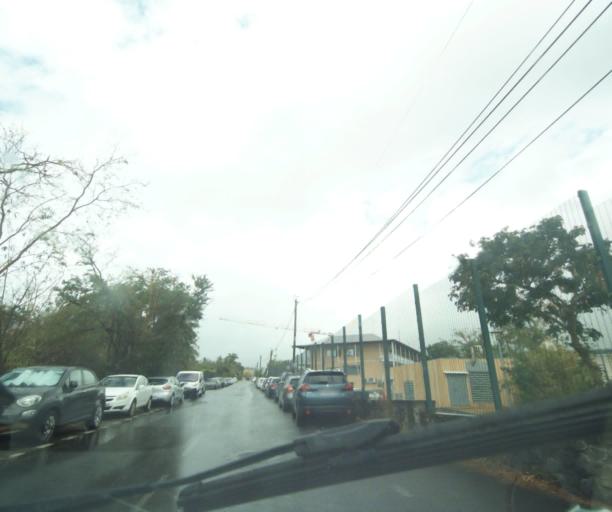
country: RE
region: Reunion
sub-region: Reunion
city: Le Port
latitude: -20.9750
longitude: 55.3011
